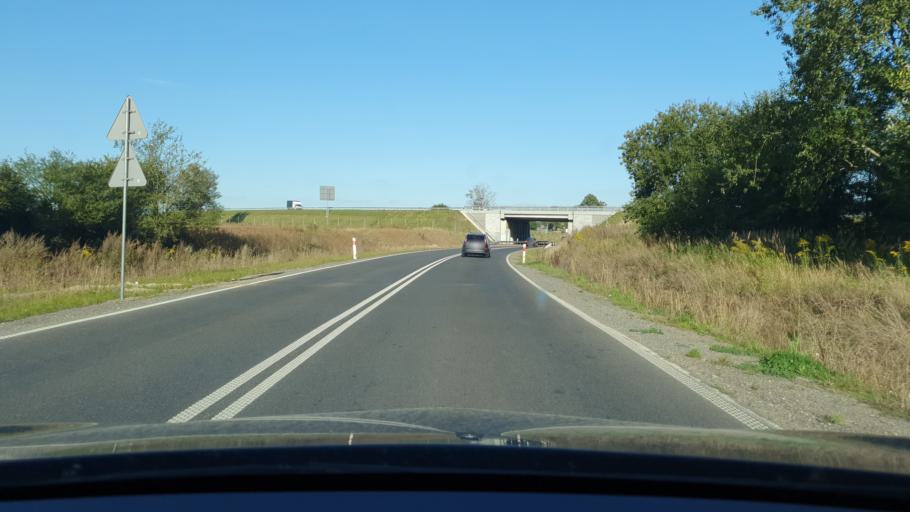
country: PL
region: West Pomeranian Voivodeship
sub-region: Powiat gryficki
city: Ploty
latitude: 53.8118
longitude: 15.2458
